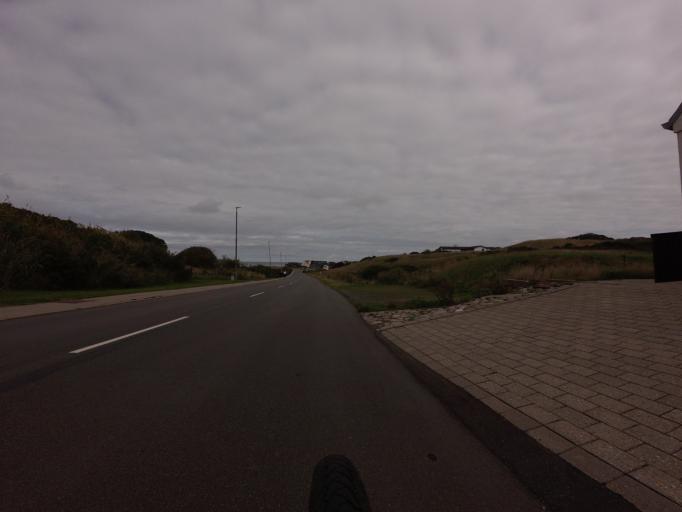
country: DK
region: North Denmark
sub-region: Hjorring Kommune
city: Hirtshals
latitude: 57.5845
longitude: 9.9460
